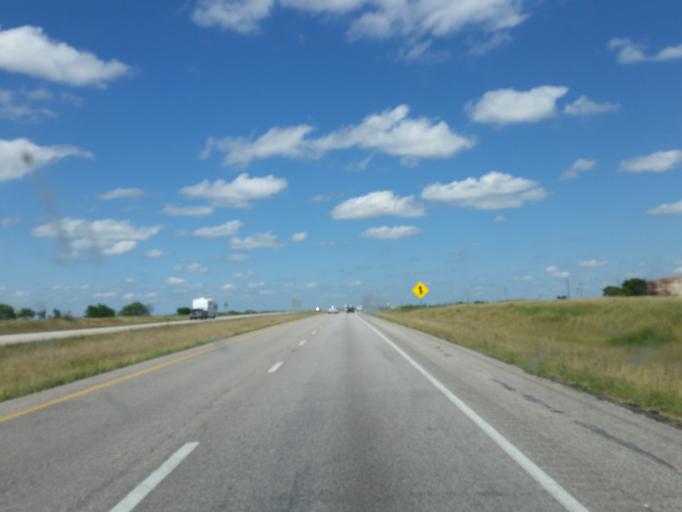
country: US
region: Texas
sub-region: Eastland County
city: Cisco
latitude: 32.3748
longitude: -99.1758
